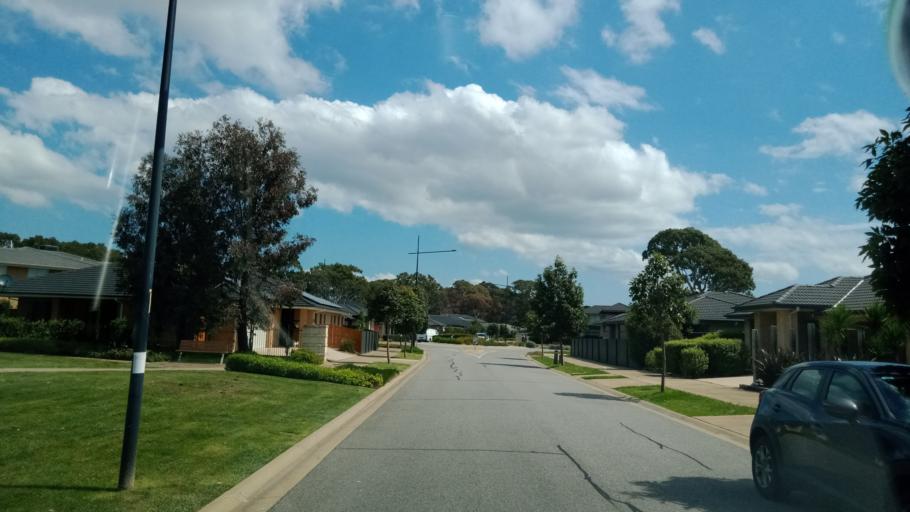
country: AU
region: Victoria
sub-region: Frankston
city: Sandhurst
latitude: -38.0870
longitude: 145.2042
